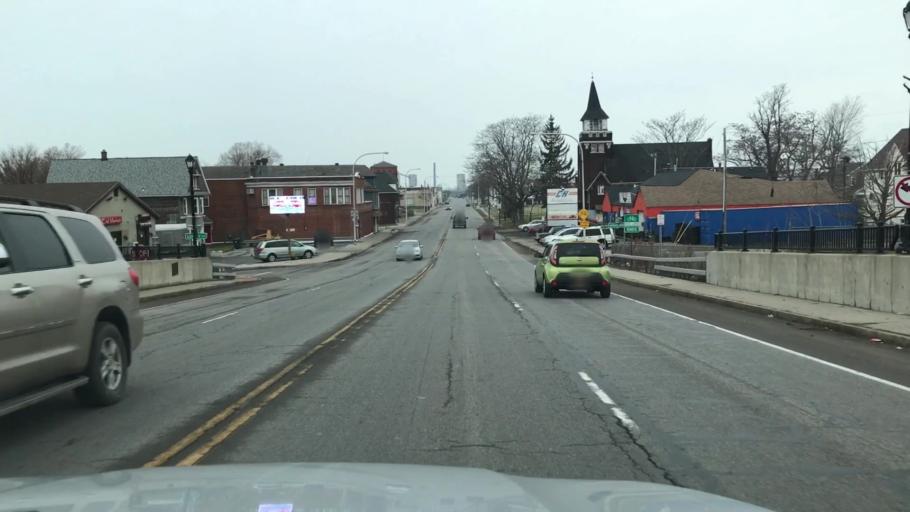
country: US
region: New York
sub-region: Erie County
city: Lackawanna
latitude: 42.8267
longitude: -78.8389
